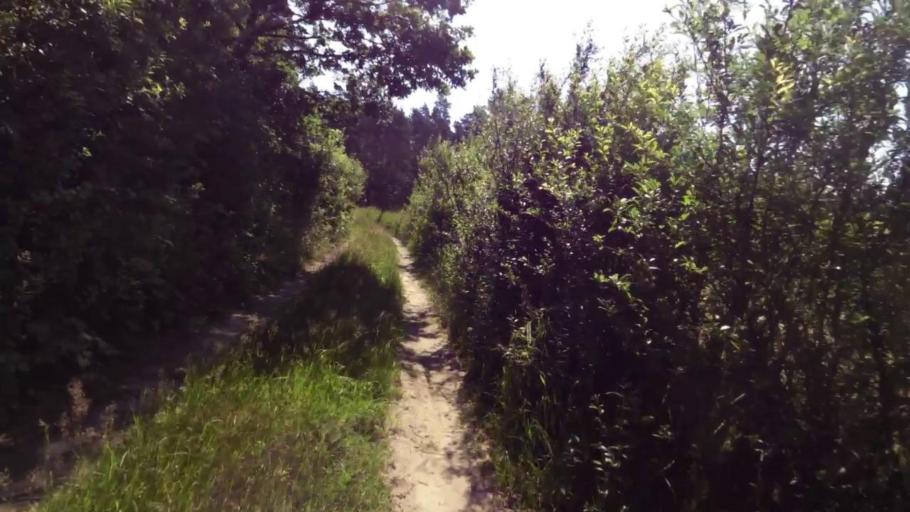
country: PL
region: West Pomeranian Voivodeship
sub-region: Powiat swidwinski
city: Polczyn-Zdroj
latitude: 53.8841
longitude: 16.0929
